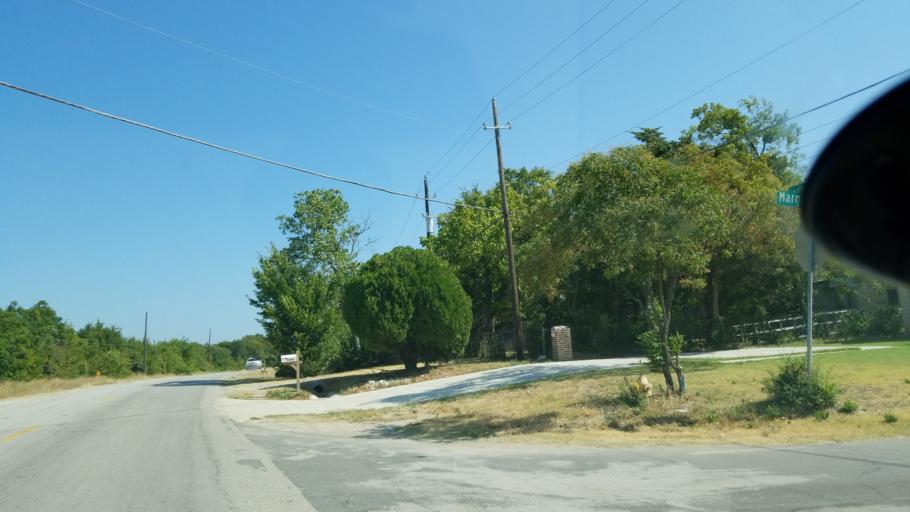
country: US
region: Texas
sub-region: Dallas County
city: Cockrell Hill
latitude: 32.7014
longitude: -96.9256
